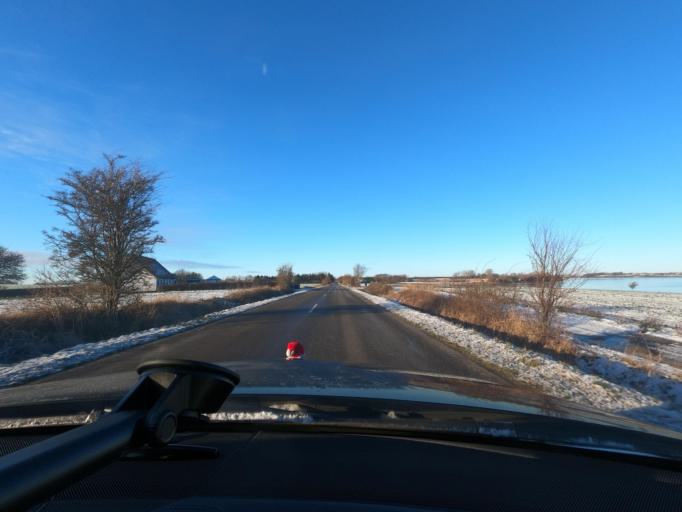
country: DK
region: South Denmark
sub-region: Sonderborg Kommune
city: Horuphav
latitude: 54.8663
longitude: 9.9580
